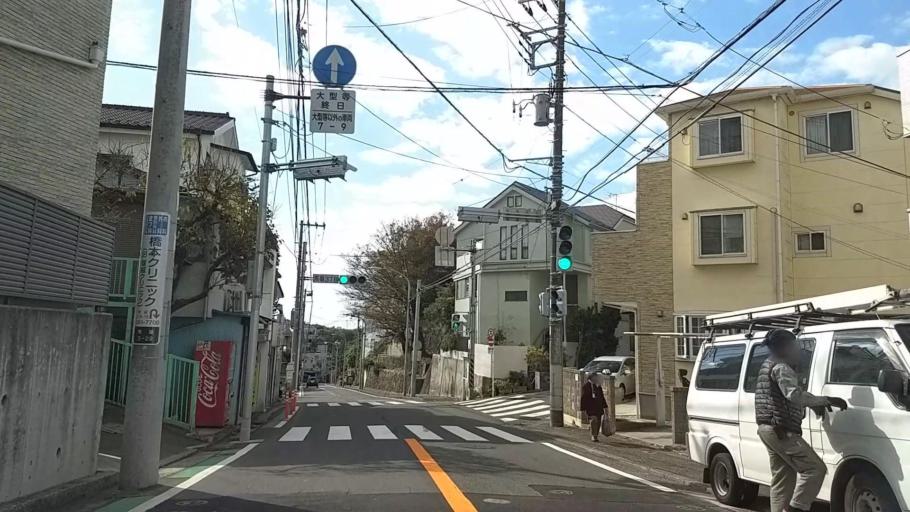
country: JP
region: Kanagawa
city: Yokohama
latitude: 35.5098
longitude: 139.6542
